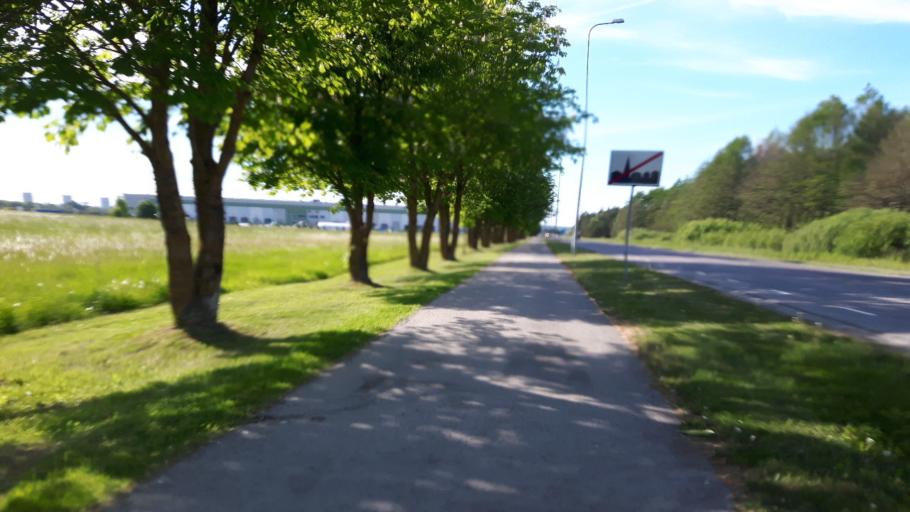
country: EE
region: Harju
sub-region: Joelaehtme vald
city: Loo
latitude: 59.4383
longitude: 24.9382
